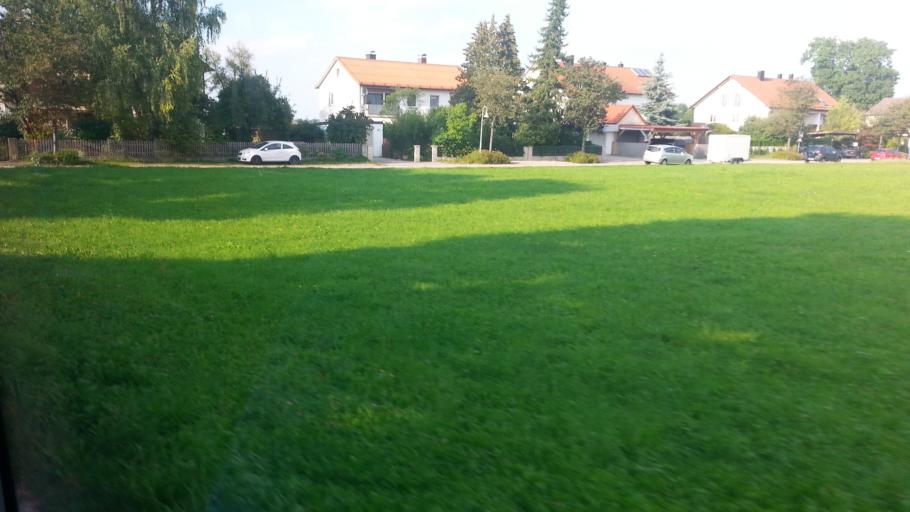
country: DE
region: Bavaria
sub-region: Upper Bavaria
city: Neufahrn bei Freising
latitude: 48.2827
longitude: 11.6735
